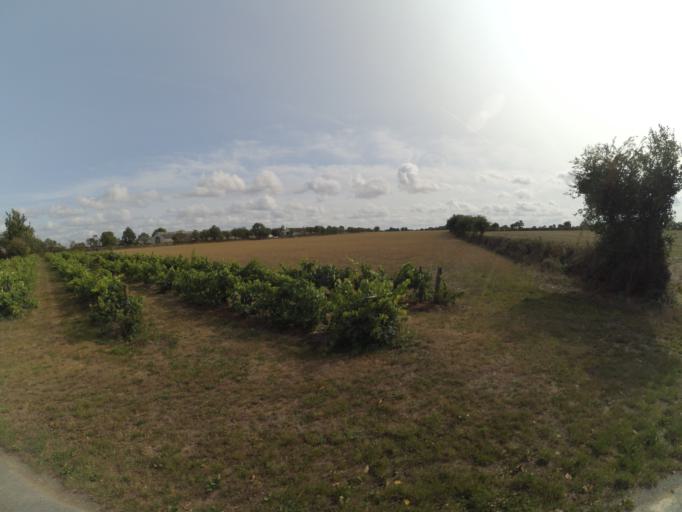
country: FR
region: Pays de la Loire
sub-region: Departement de la Vendee
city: Treize-Septiers
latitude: 46.9749
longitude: -1.2180
